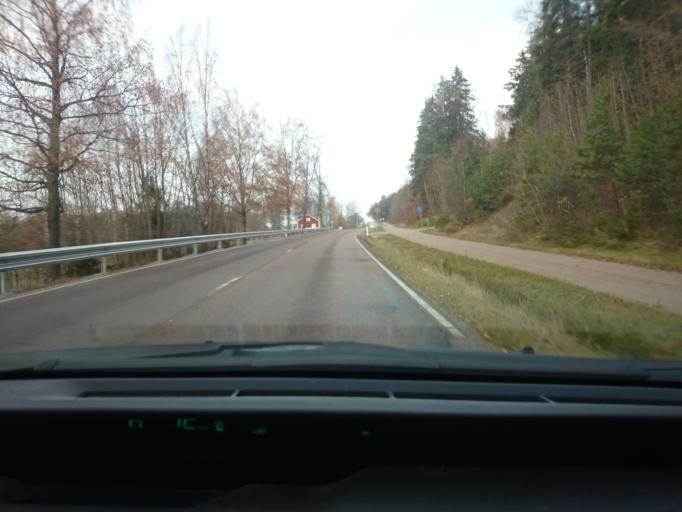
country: SE
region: Vaestmanland
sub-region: Vasteras
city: Skultuna
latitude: 59.6720
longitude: 16.4731
